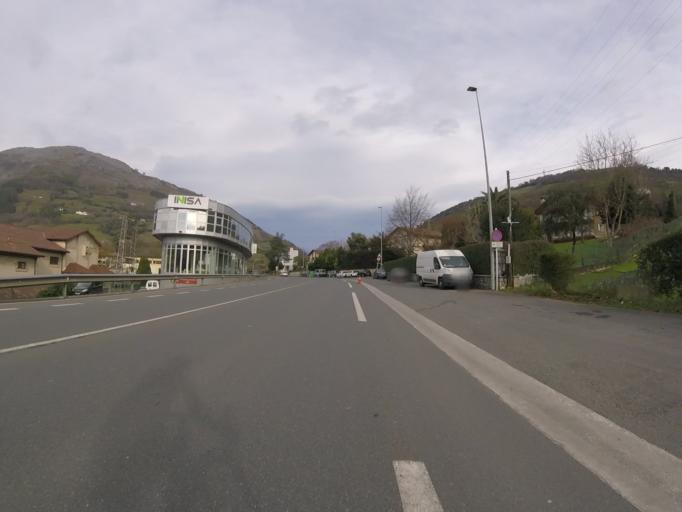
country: ES
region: Basque Country
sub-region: Provincia de Guipuzcoa
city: Azpeitia
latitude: 43.1836
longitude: -2.2601
